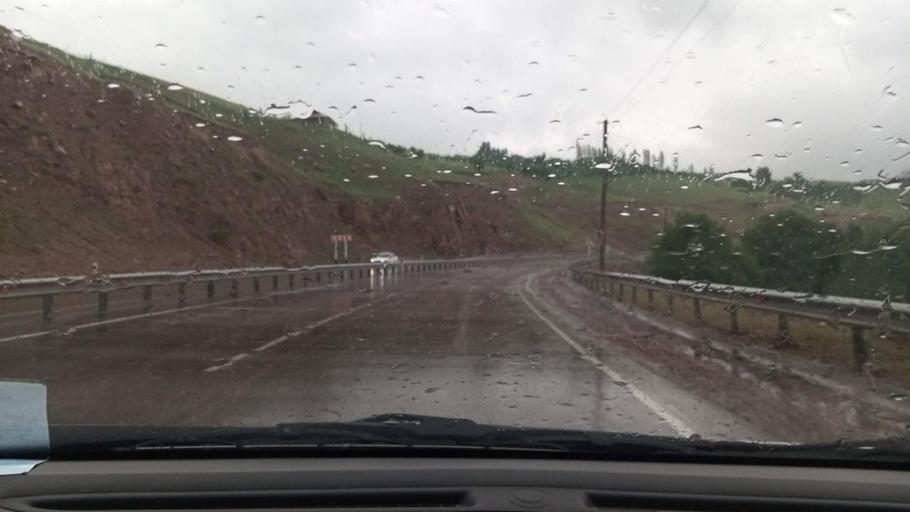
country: UZ
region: Toshkent
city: Angren
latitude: 41.0981
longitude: 70.3228
